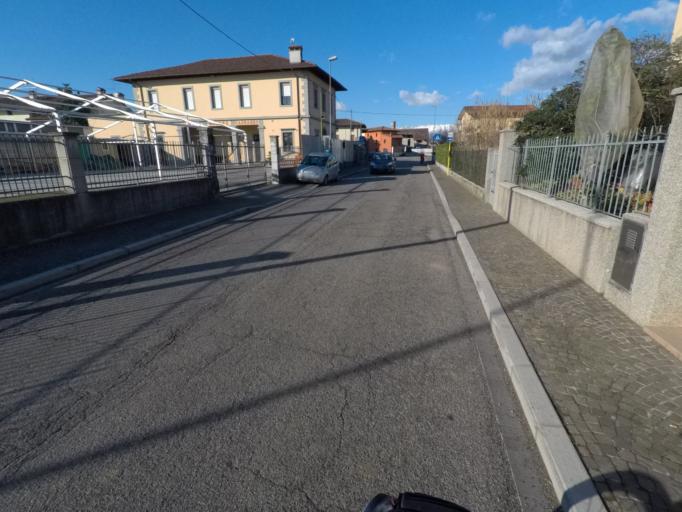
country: IT
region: Friuli Venezia Giulia
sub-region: Provincia di Udine
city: Povoletto
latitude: 46.1030
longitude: 13.3066
